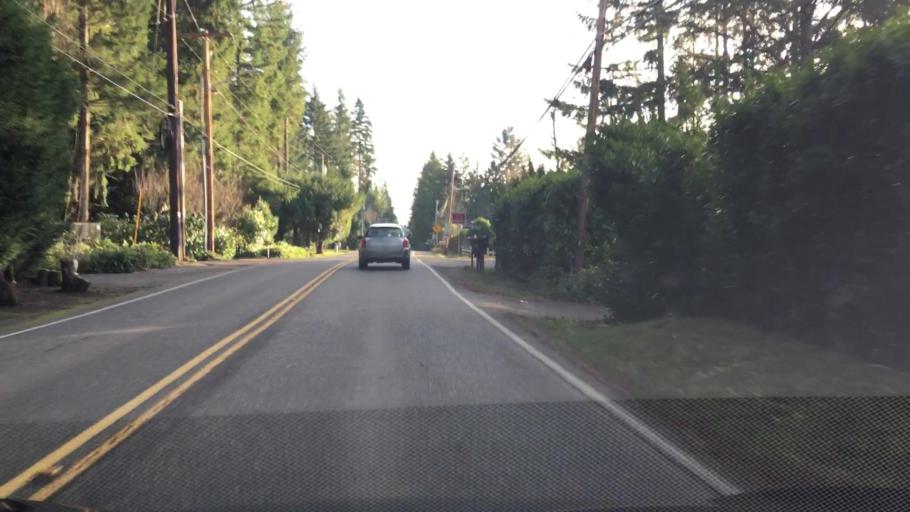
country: US
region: Washington
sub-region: Snohomish County
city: Maltby
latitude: 47.7764
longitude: -122.1319
